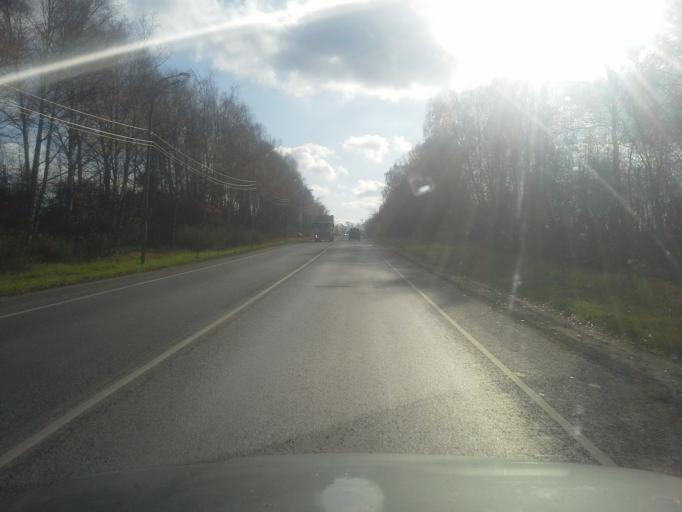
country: RU
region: Moskovskaya
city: Zvenigorod
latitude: 55.6871
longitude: 36.8989
